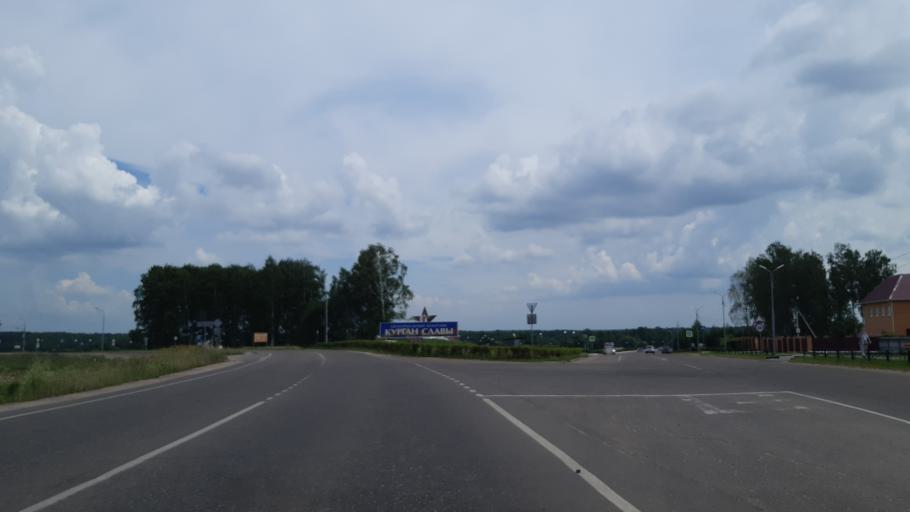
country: RU
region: Smolensk
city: Desnogorsk
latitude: 54.1552
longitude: 33.3035
